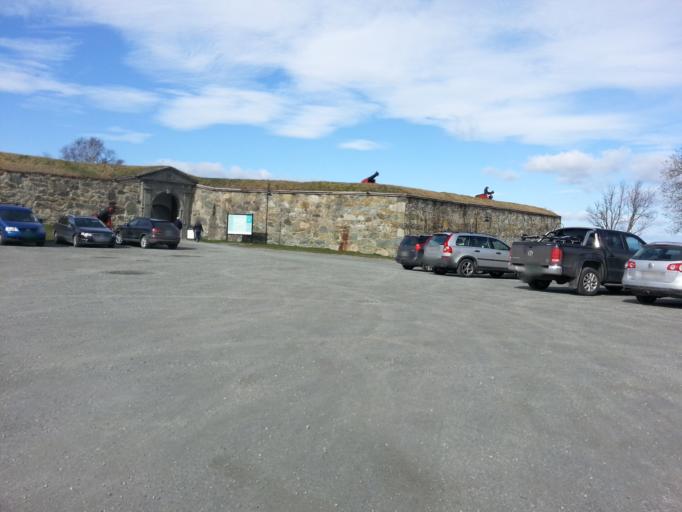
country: NO
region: Sor-Trondelag
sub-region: Trondheim
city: Trondheim
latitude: 63.4266
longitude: 10.4122
